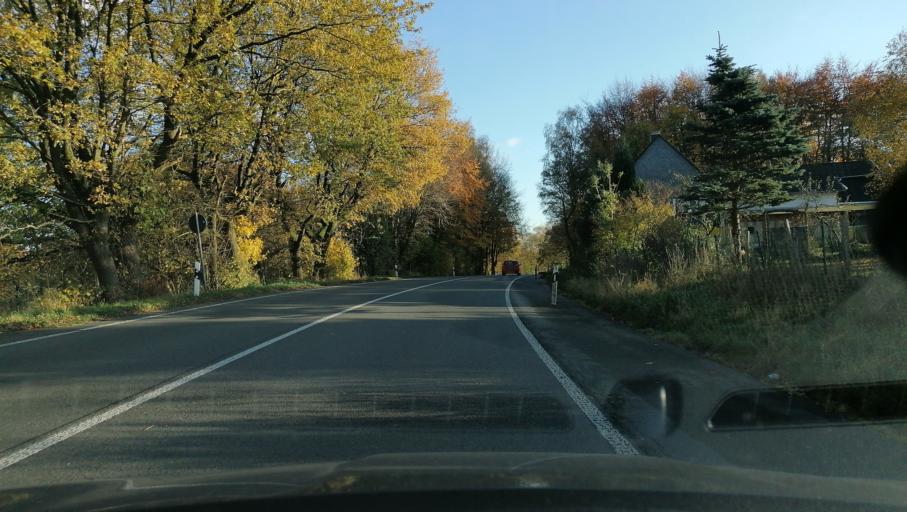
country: DE
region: North Rhine-Westphalia
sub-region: Regierungsbezirk Arnsberg
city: Schwelm
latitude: 51.2755
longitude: 7.3121
